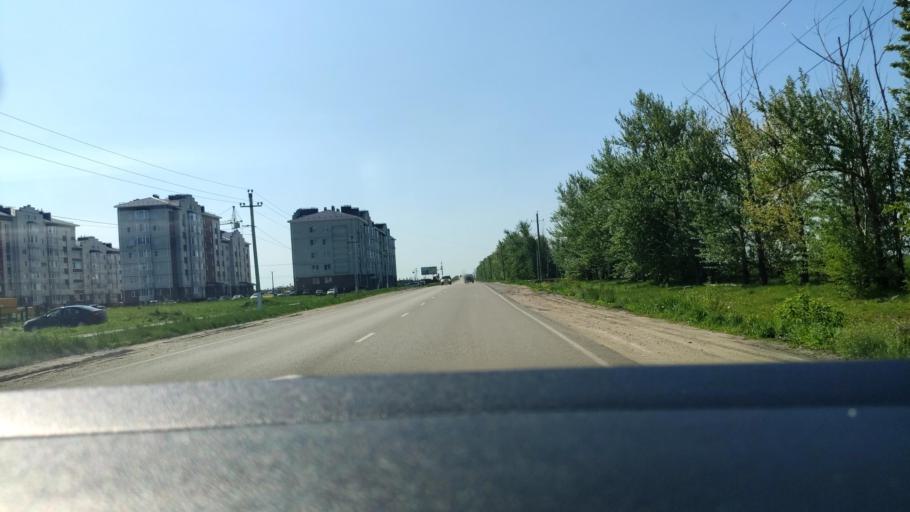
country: RU
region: Voronezj
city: Novaya Usman'
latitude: 51.6037
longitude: 39.3731
